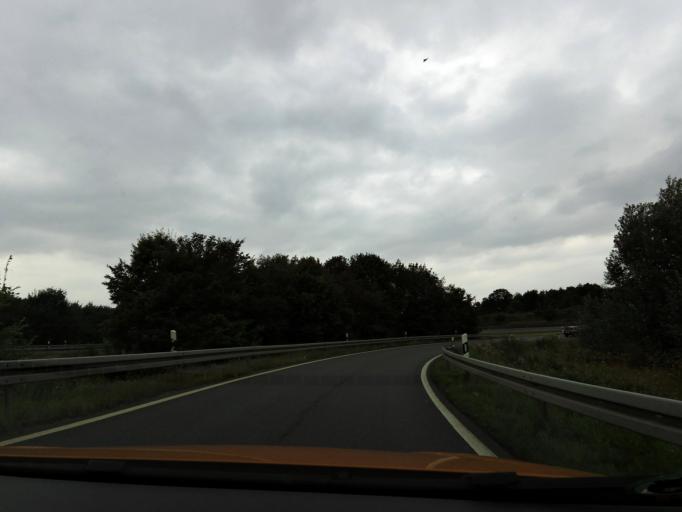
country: DE
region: Lower Saxony
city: Klein Schwulper
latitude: 52.3339
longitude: 10.4218
